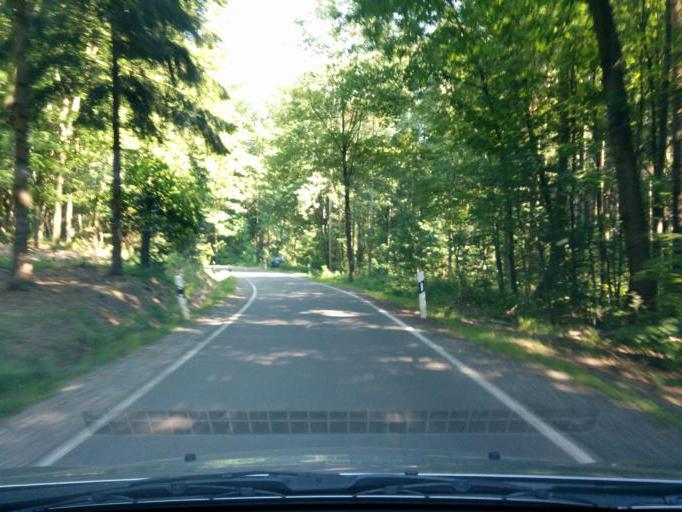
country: DE
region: Saxony
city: Floha
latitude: 50.8426
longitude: 13.0431
